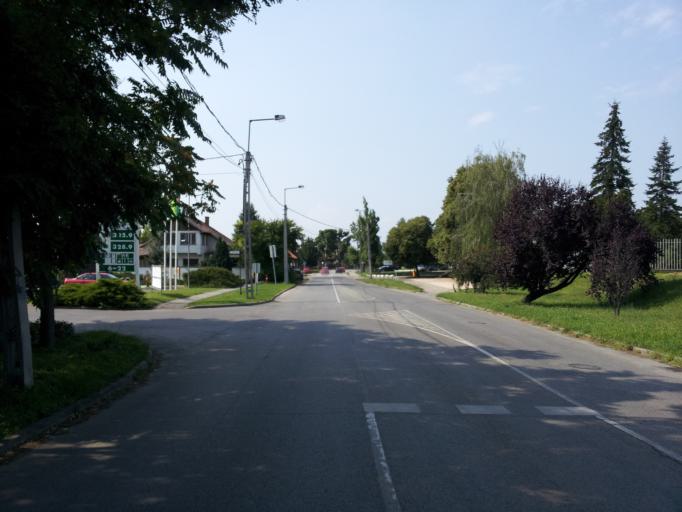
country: HU
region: Pest
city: Rackeve
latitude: 47.1717
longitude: 18.9440
